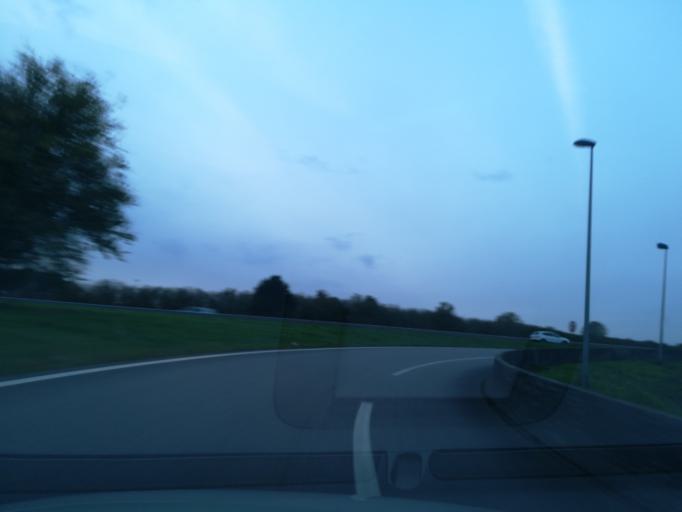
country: FR
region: Haute-Normandie
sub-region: Departement de la Seine-Maritime
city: Bois-Guillaume
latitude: 49.4772
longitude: 1.1386
